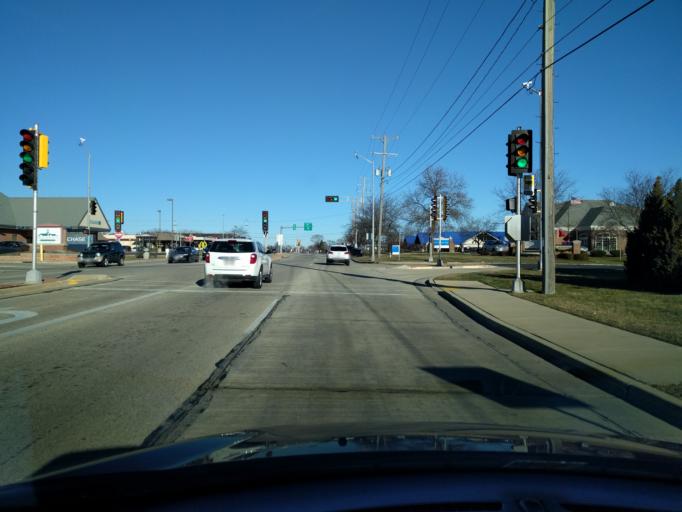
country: US
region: Wisconsin
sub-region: Milwaukee County
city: River Hills
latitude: 43.1747
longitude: -87.9126
